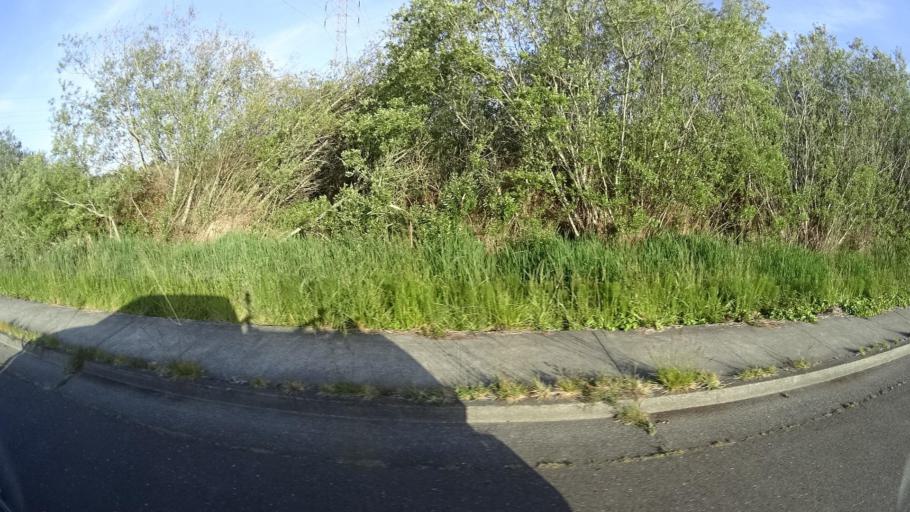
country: US
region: California
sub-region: Humboldt County
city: Humboldt Hill
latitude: 40.7384
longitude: -124.2003
